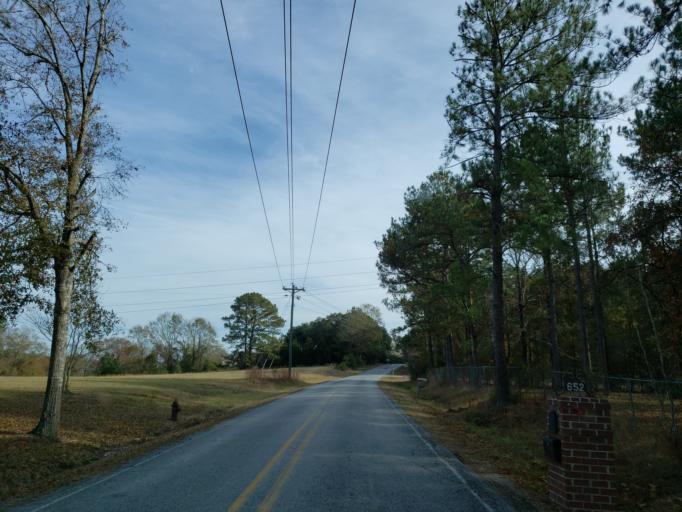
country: US
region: Mississippi
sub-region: Forrest County
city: Rawls Springs
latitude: 31.4112
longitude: -89.4096
